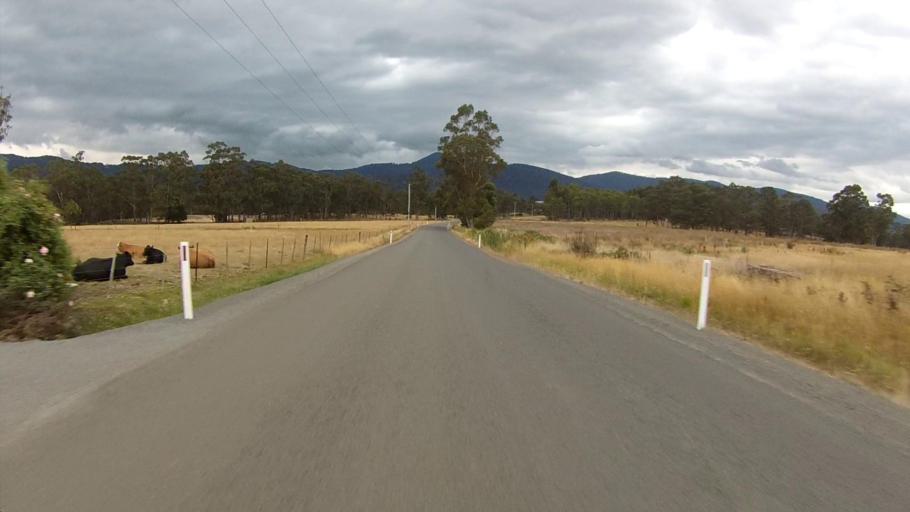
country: AU
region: Tasmania
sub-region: Huon Valley
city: Huonville
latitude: -42.9631
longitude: 147.0814
